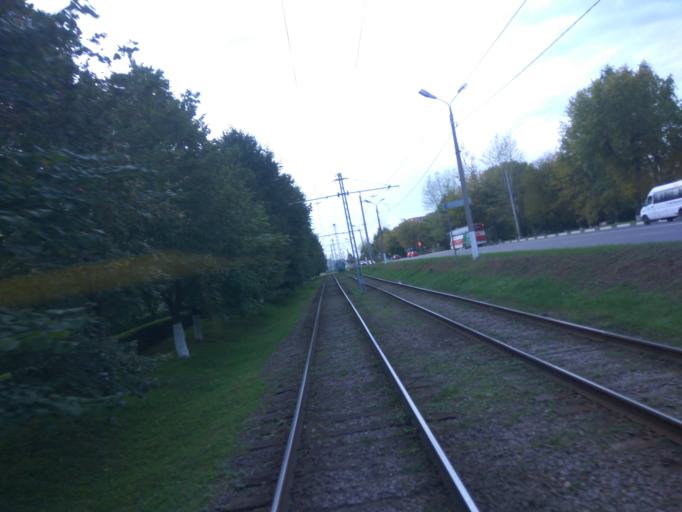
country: RU
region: Moskovskaya
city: Kolomna
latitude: 55.0913
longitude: 38.7777
